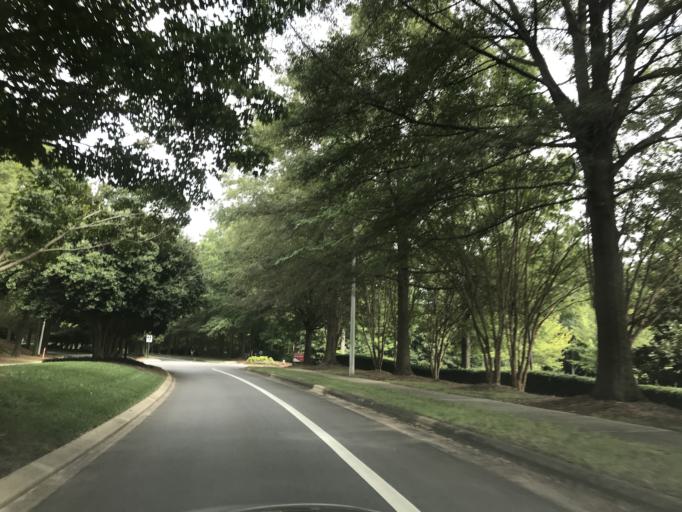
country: US
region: North Carolina
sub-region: Wake County
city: Cary
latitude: 35.7322
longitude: -78.7841
